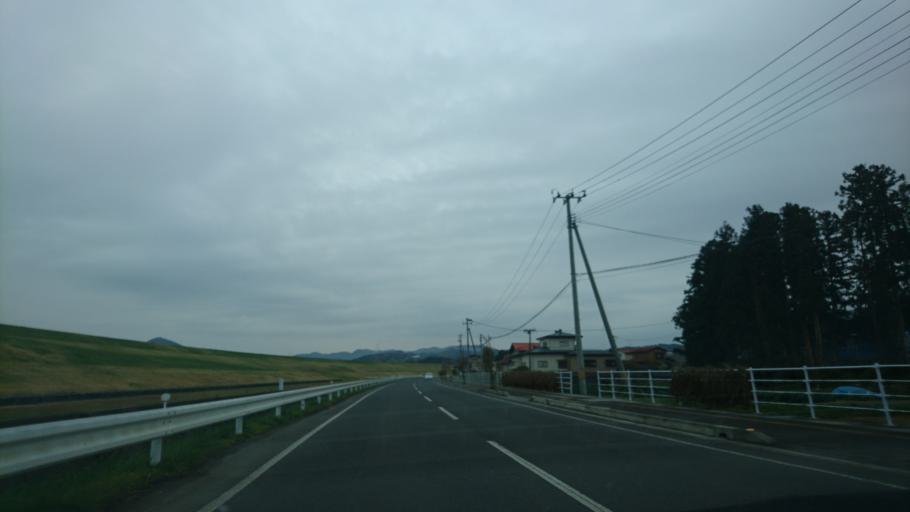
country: JP
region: Iwate
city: Ichinoseki
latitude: 38.9428
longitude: 141.1490
